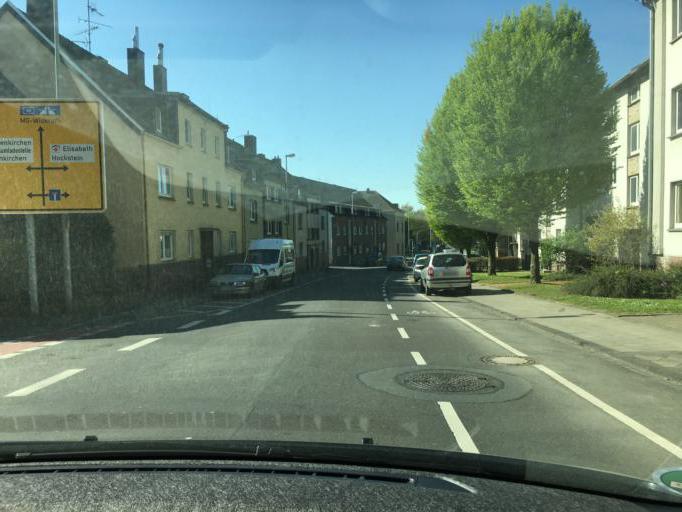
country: DE
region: North Rhine-Westphalia
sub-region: Regierungsbezirk Dusseldorf
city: Monchengladbach
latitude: 51.1510
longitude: 6.4336
